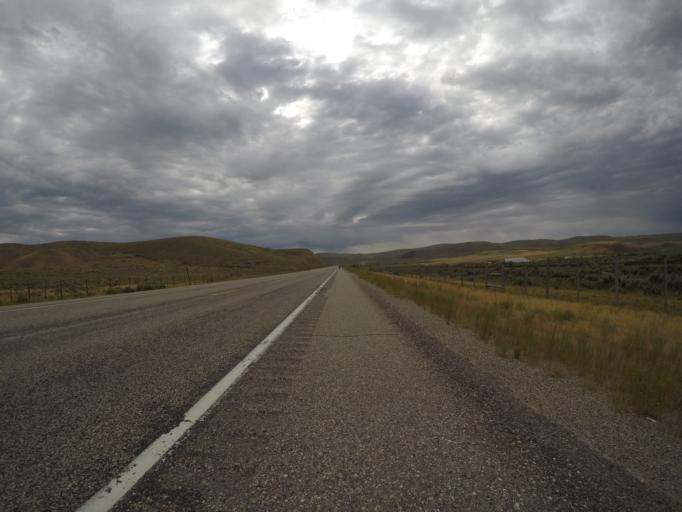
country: US
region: Utah
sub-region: Rich County
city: Randolph
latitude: 41.8228
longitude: -110.8948
